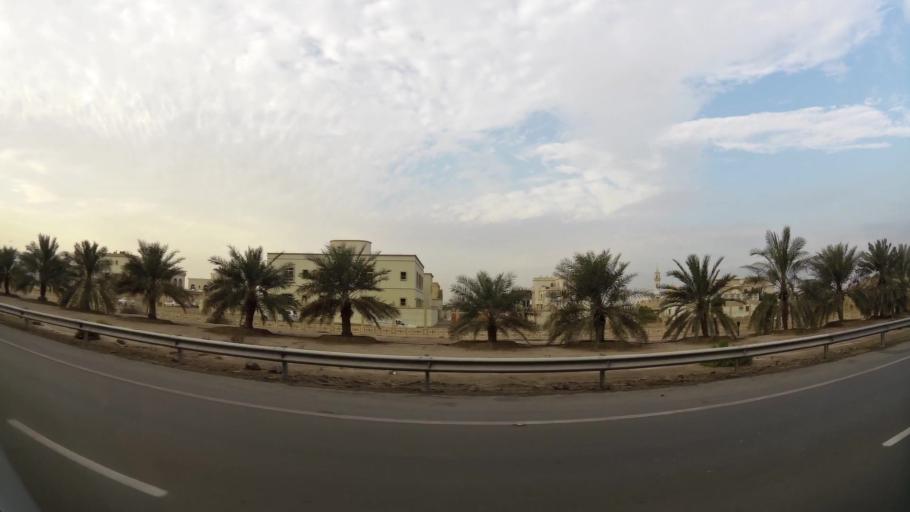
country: AE
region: Abu Dhabi
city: Abu Dhabi
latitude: 24.2903
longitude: 54.6357
